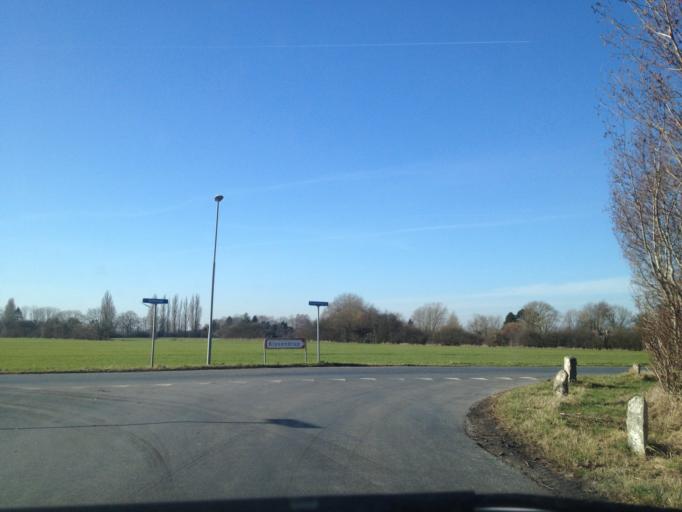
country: DK
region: South Denmark
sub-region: Nyborg Kommune
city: Ullerslev
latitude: 55.3832
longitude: 10.7125
